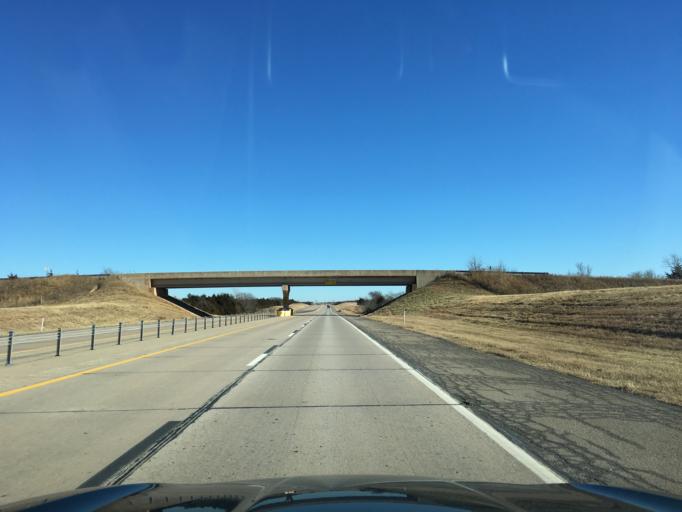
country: US
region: Oklahoma
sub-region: Pawnee County
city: Pawnee
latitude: 36.2249
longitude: -96.8383
